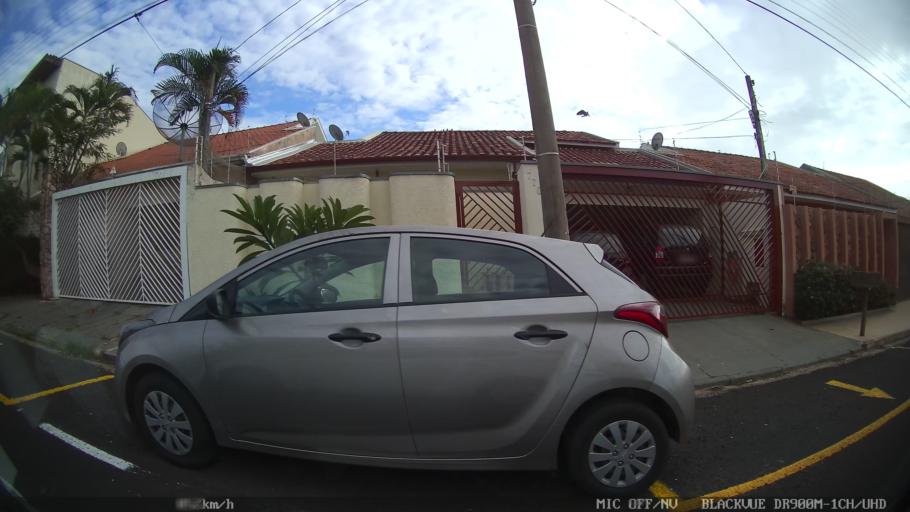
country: BR
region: Sao Paulo
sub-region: Sao Jose Do Rio Preto
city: Sao Jose do Rio Preto
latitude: -20.8260
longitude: -49.4119
